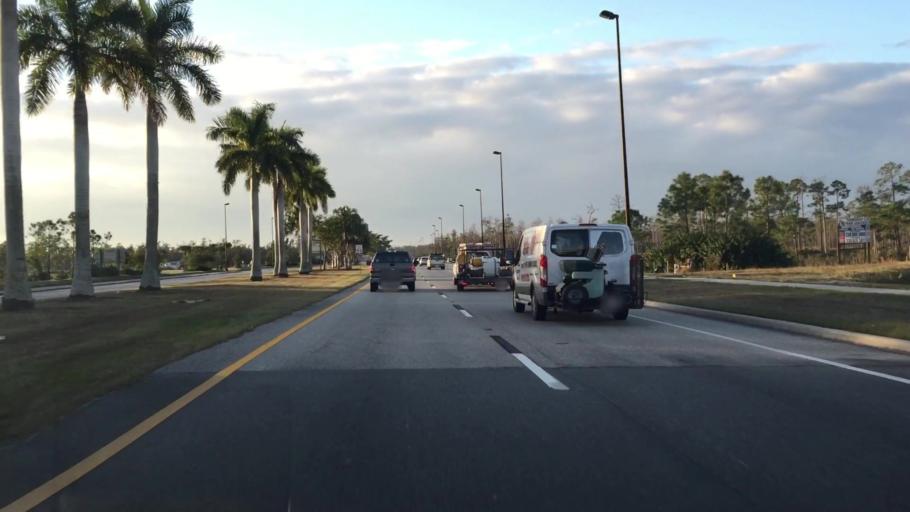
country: US
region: Florida
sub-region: Lee County
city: Three Oaks
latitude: 26.5112
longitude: -81.7856
